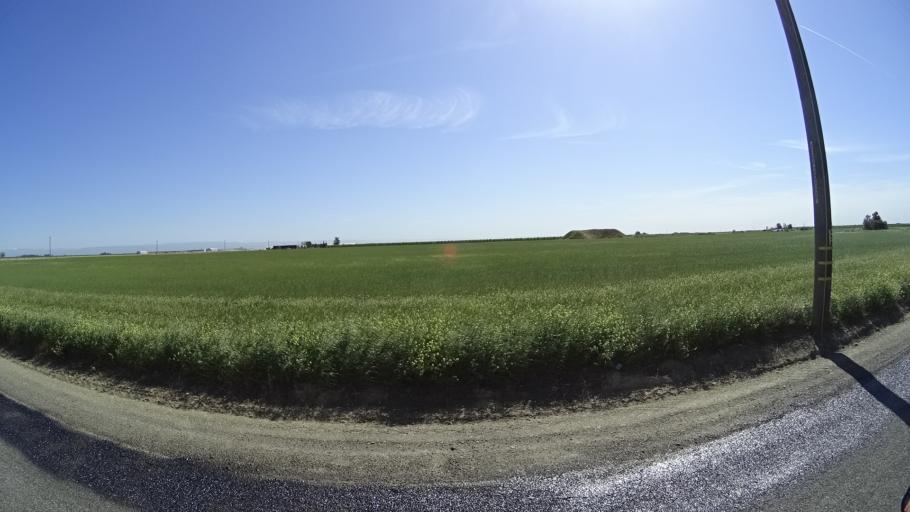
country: US
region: California
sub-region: Glenn County
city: Orland
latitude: 39.6525
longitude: -122.1785
